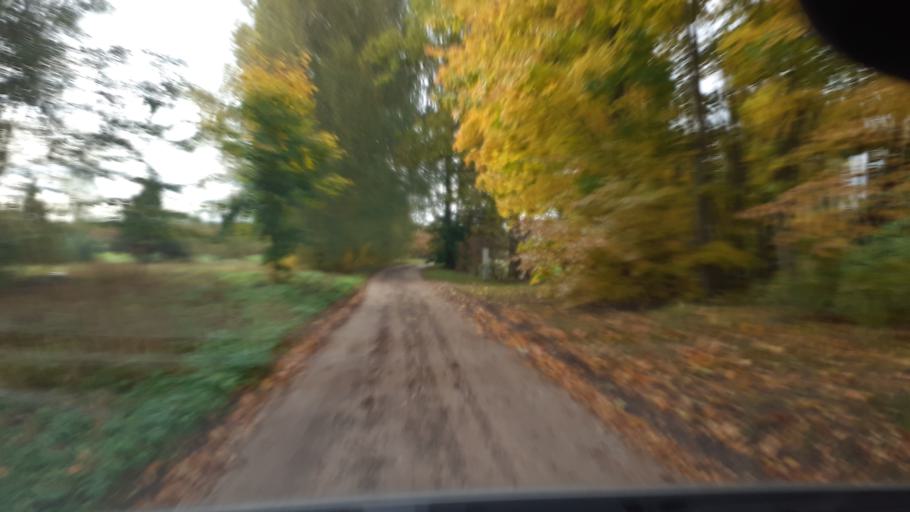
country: LV
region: Kuldigas Rajons
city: Kuldiga
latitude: 56.9732
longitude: 21.9393
